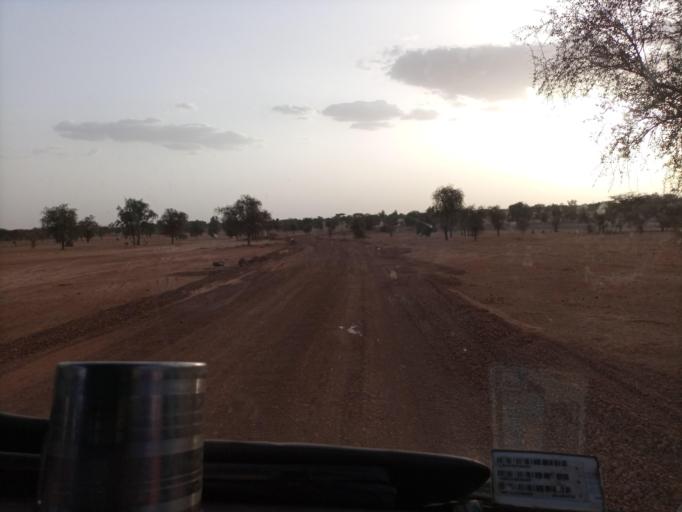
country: SN
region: Louga
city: Dara
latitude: 15.3780
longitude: -15.5974
